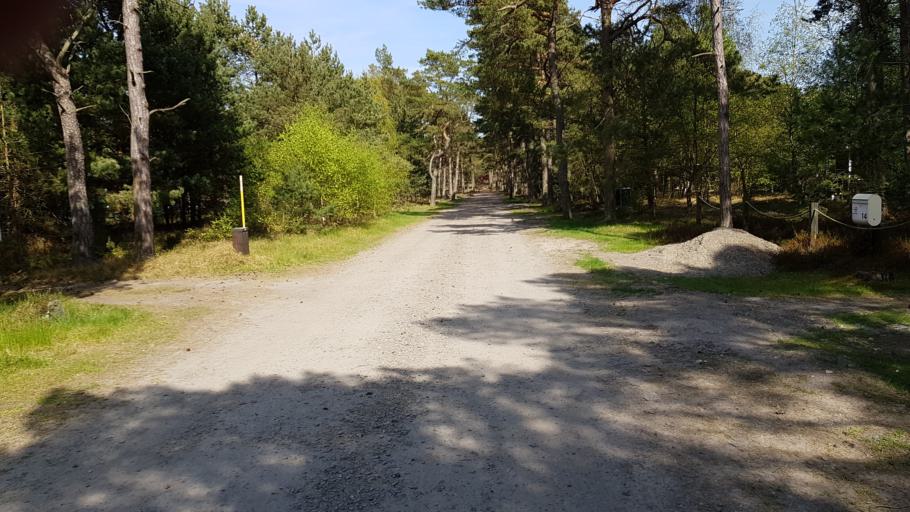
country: DK
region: Capital Region
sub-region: Bornholm Kommune
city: Nexo
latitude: 54.9942
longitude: 15.0823
